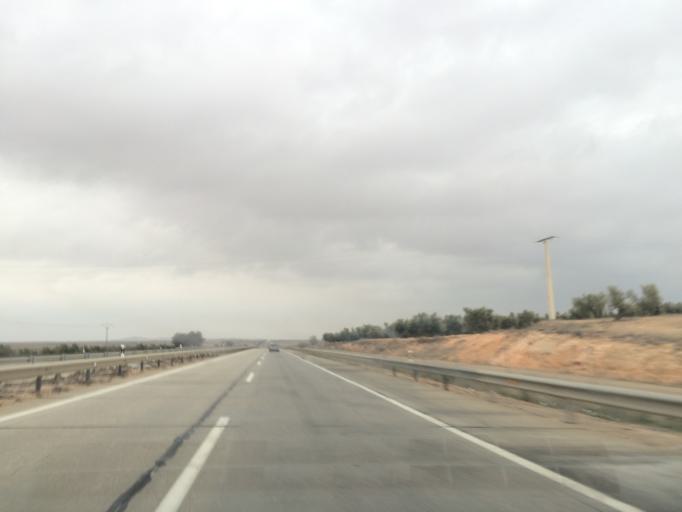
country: ES
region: Castille-La Mancha
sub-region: Province of Toledo
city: Madridejos
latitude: 39.5318
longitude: -3.5208
